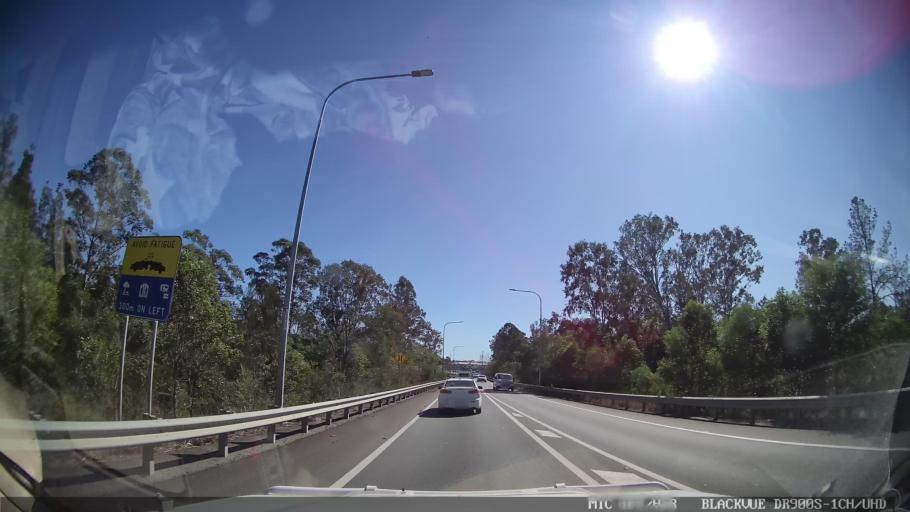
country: AU
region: Queensland
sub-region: Gympie Regional Council
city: Monkland
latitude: -26.2339
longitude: 152.6982
